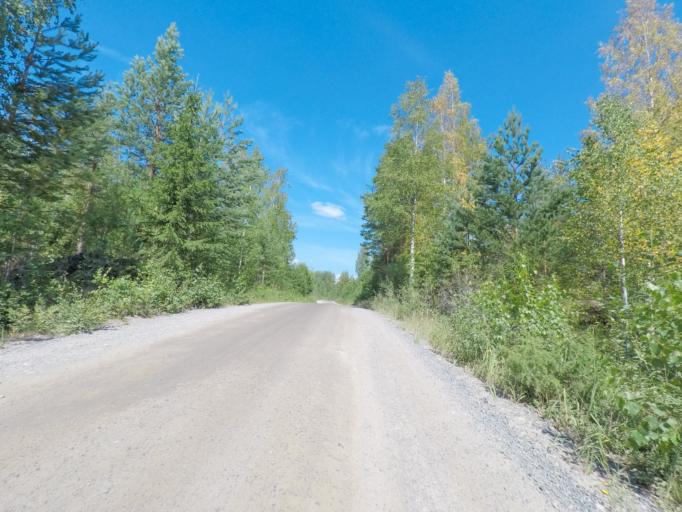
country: FI
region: Southern Savonia
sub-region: Mikkeli
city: Puumala
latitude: 61.4095
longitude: 28.0477
